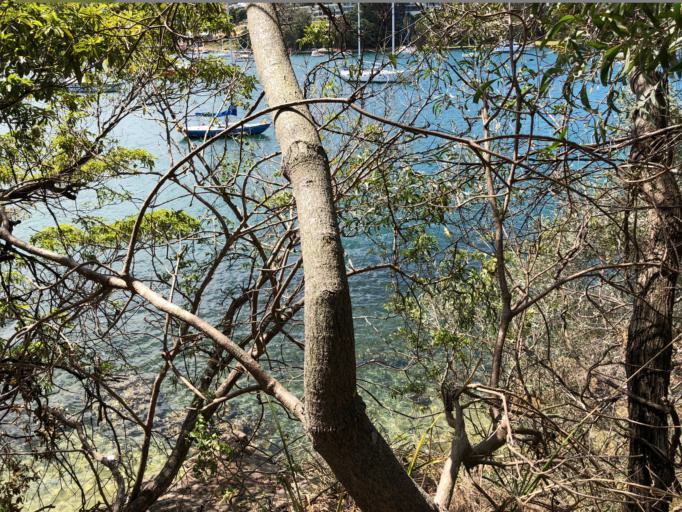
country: AU
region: New South Wales
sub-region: Leichhardt
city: Balmain East
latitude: -33.8467
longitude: 151.1978
